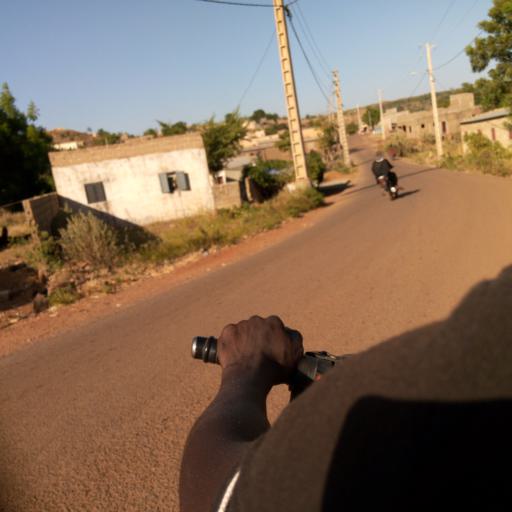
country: ML
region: Bamako
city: Bamako
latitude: 12.6557
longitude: -8.0407
